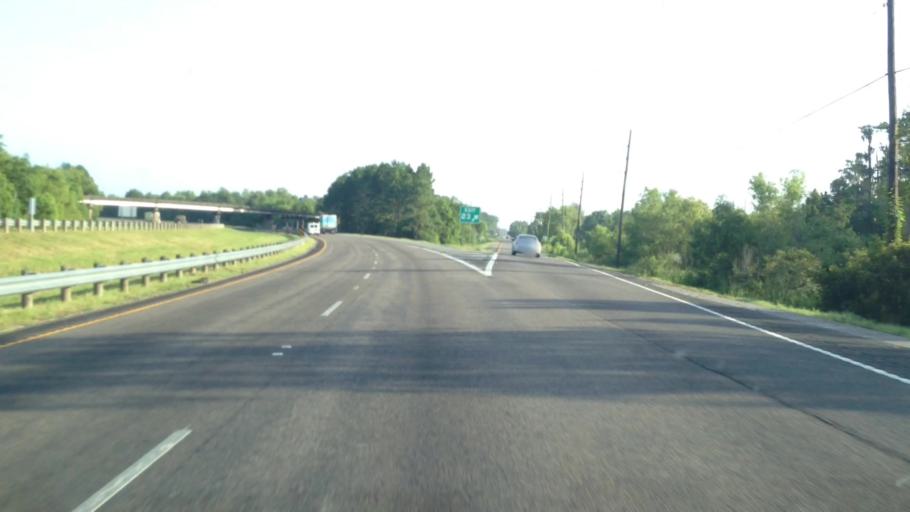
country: US
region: Louisiana
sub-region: Tangipahoa Parish
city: Ponchatoula
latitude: 30.4107
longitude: -90.4332
